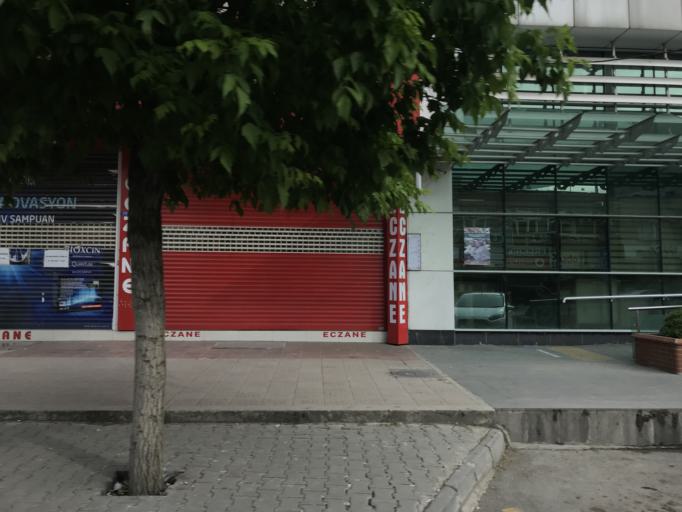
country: TR
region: Gaziantep
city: Sahinbey
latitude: 37.0526
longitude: 37.3359
